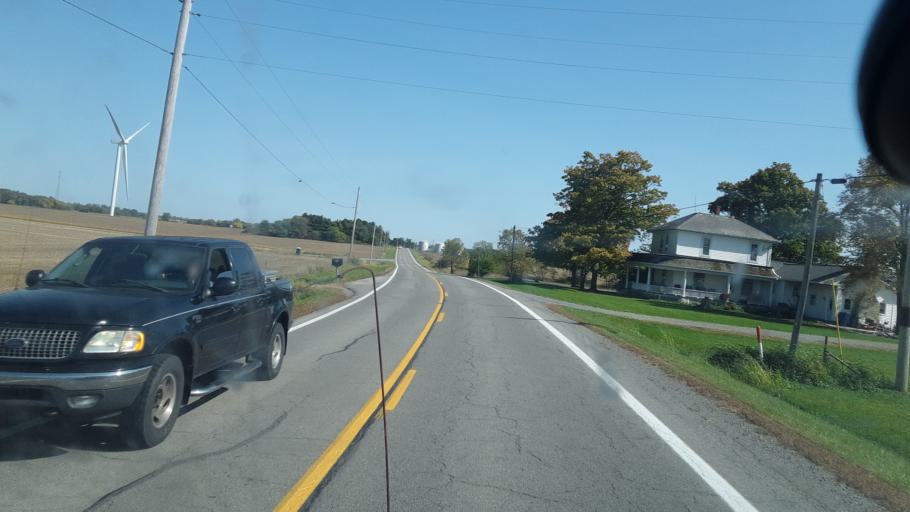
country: US
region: Ohio
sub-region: Logan County
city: Northwood
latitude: 40.5033
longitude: -83.7110
